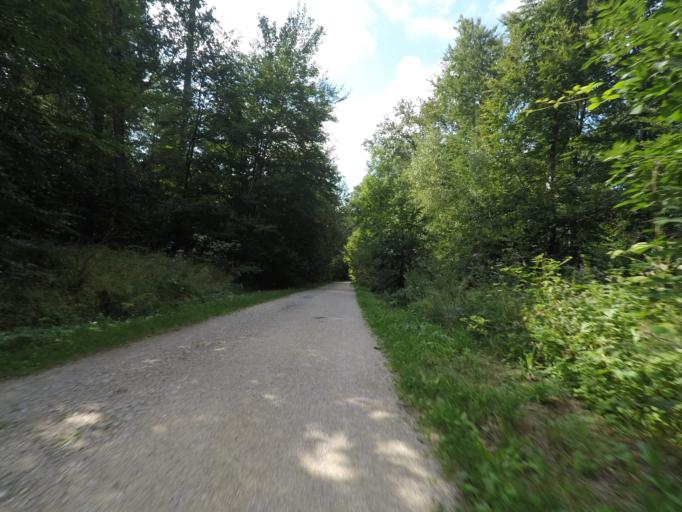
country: DE
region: Baden-Wuerttemberg
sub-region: Regierungsbezirk Stuttgart
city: Altbach
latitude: 48.7473
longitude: 9.3671
